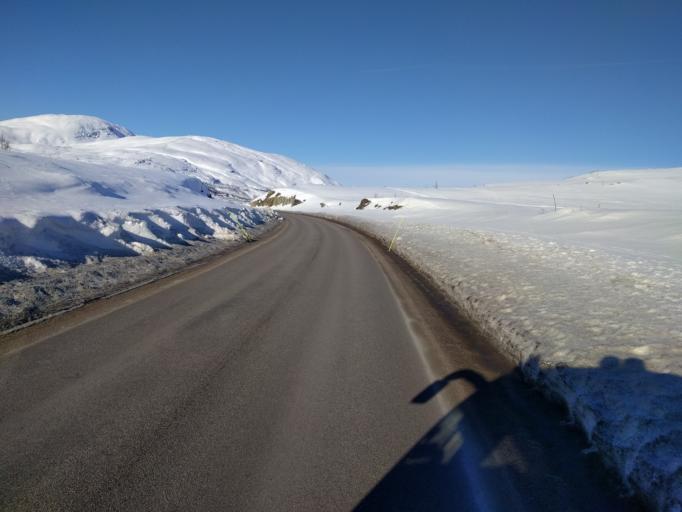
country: NO
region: Troms
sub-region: Bardu
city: Setermoen
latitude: 68.4308
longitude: 18.2012
